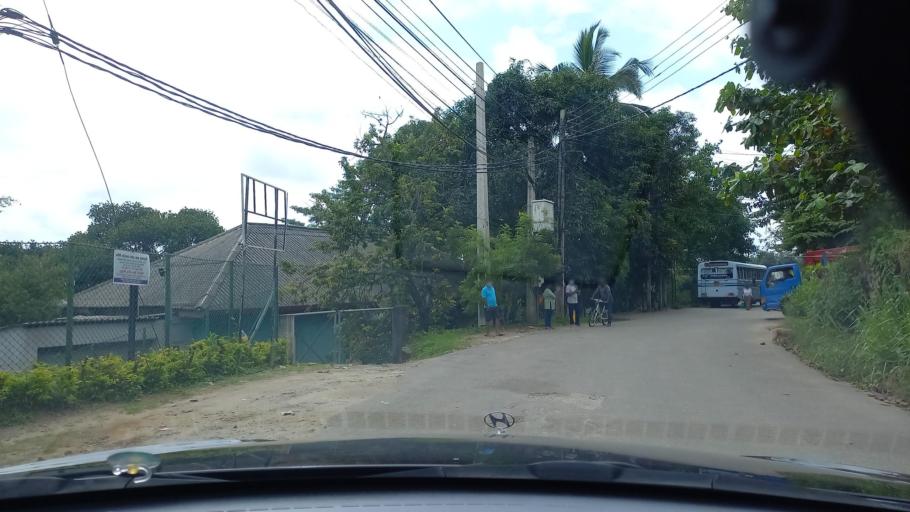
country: LK
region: Central
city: Kandy
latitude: 7.2302
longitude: 80.6053
